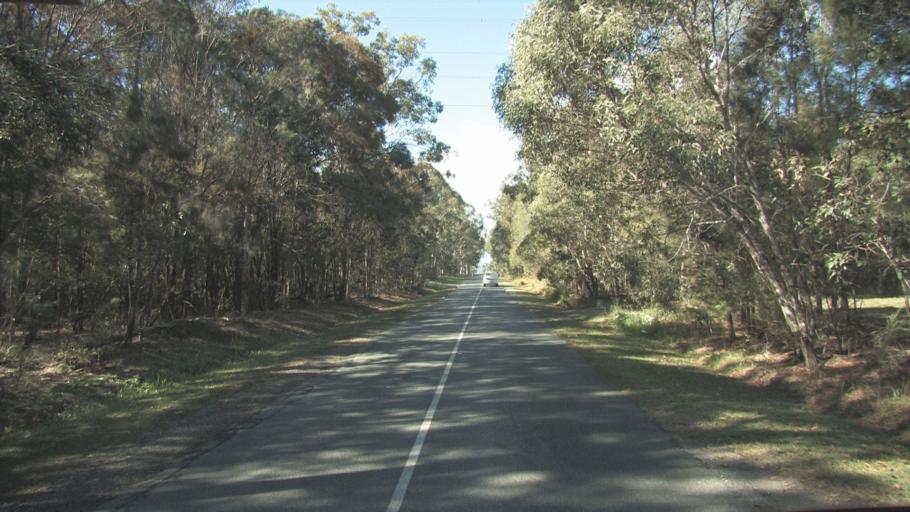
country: AU
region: Queensland
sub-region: Logan
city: Chambers Flat
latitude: -27.7920
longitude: 153.0779
